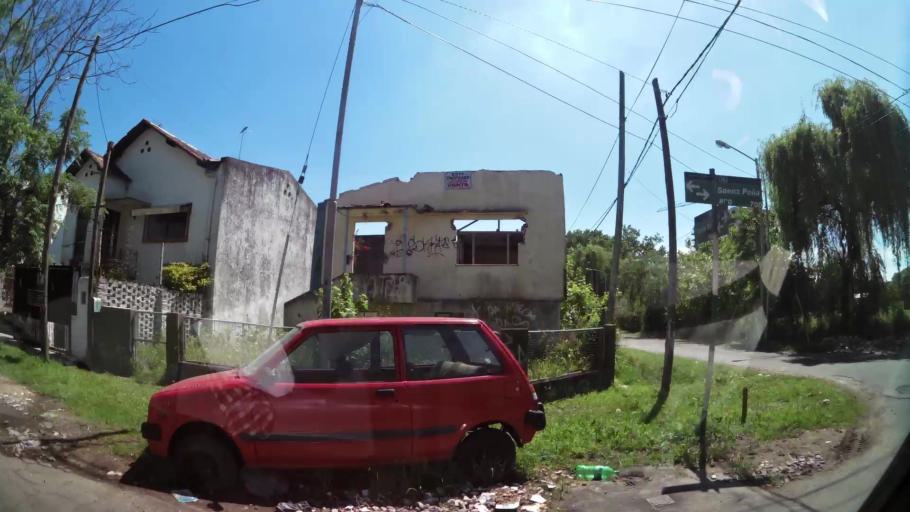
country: AR
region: Buenos Aires
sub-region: Partido de Tigre
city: Tigre
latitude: -34.4257
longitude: -58.5695
